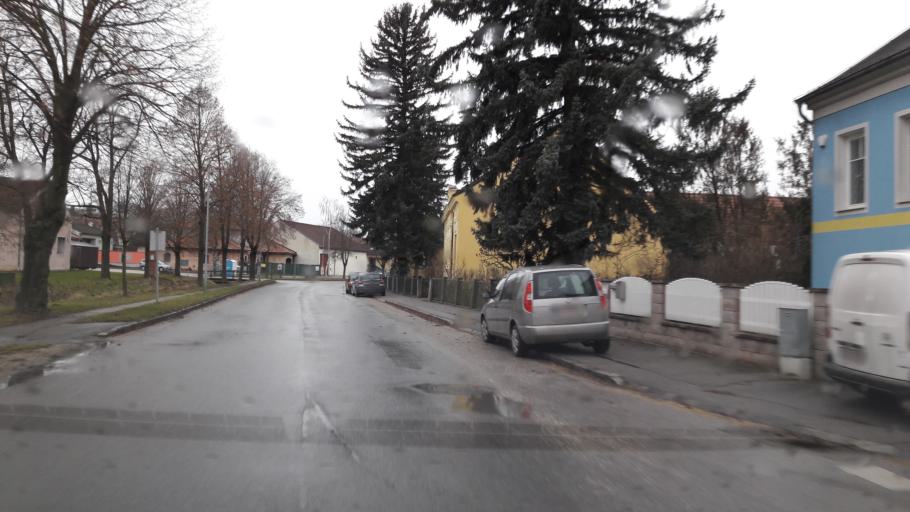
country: AT
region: Lower Austria
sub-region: Politischer Bezirk Mistelbach
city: Hochleithen
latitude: 48.4447
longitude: 16.5233
